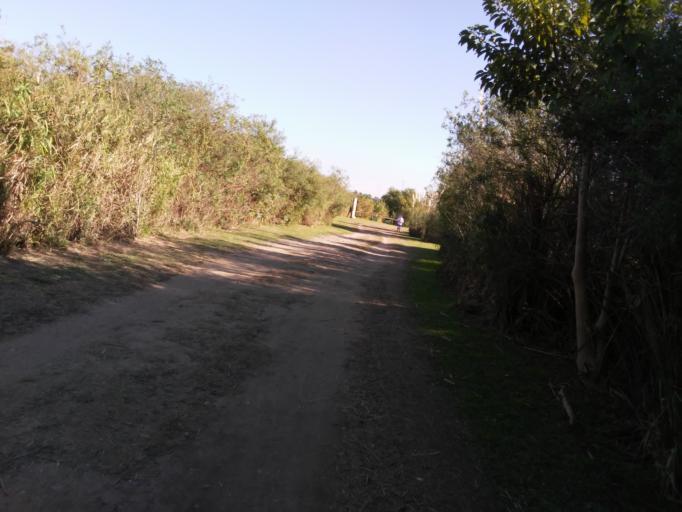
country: AR
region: Buenos Aires F.D.
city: Buenos Aires
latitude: -34.6165
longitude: -58.3407
